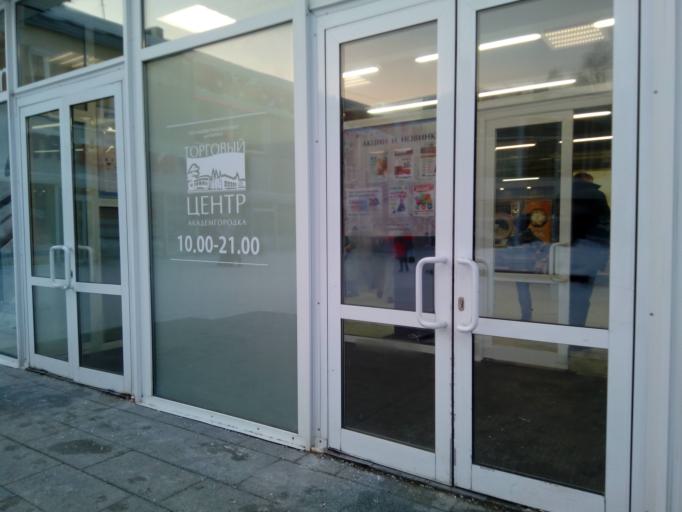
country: RU
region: Novosibirsk
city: Akademgorodok
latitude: 54.8390
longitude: 83.0959
